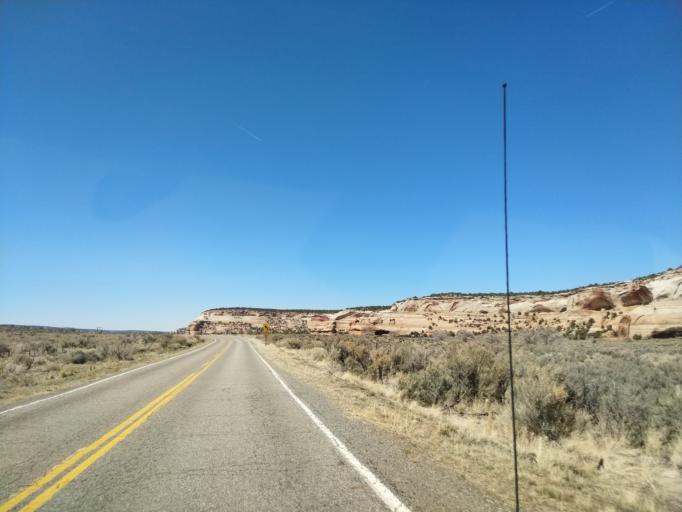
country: US
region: Colorado
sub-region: Mesa County
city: Loma
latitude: 38.9967
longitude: -108.8669
